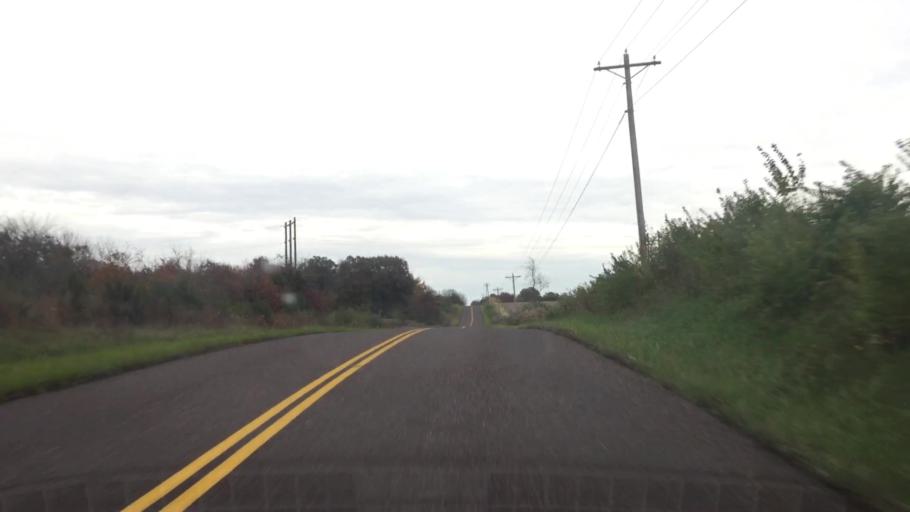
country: US
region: Missouri
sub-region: Boone County
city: Ashland
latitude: 38.8108
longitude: -92.2618
